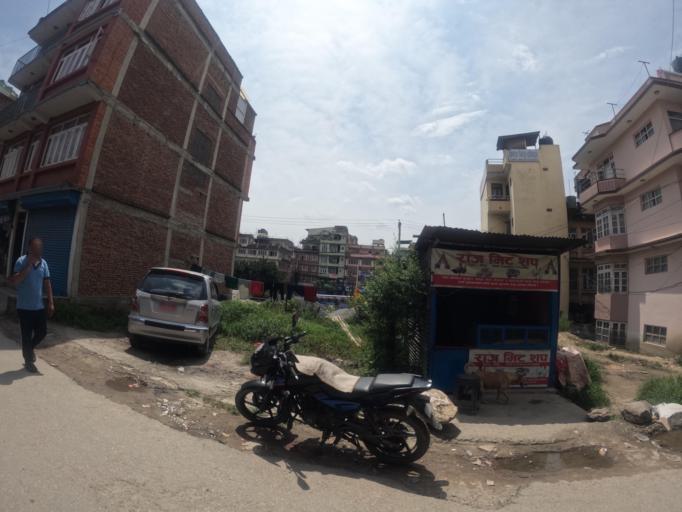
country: NP
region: Central Region
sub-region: Bagmati Zone
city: Bhaktapur
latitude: 27.6743
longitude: 85.3752
